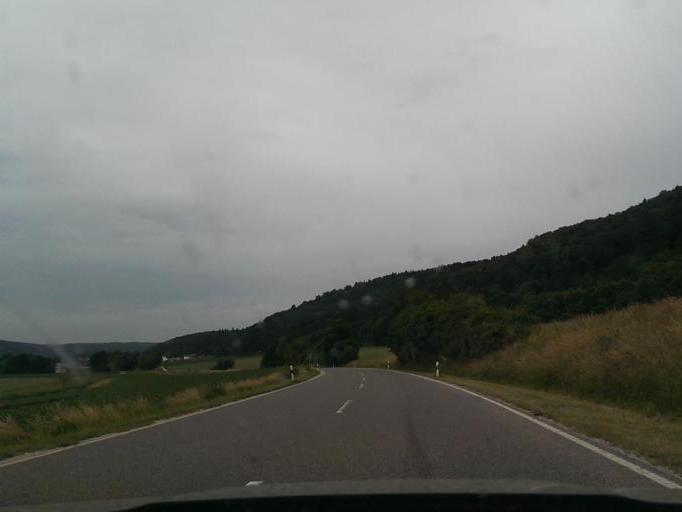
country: DE
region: Bavaria
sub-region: Upper Palatinate
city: Berching
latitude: 49.0294
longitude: 11.4531
